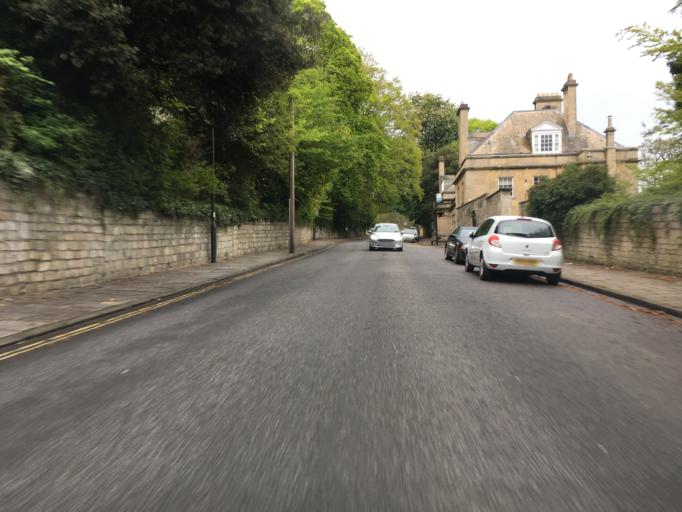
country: GB
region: England
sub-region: Bath and North East Somerset
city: Bath
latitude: 51.3789
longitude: -2.3410
